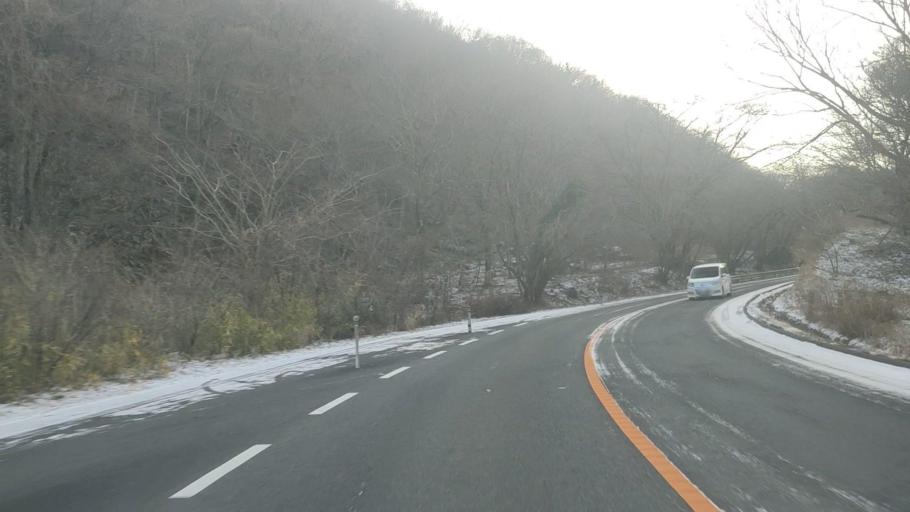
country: JP
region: Oita
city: Beppu
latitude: 33.2681
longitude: 131.4077
